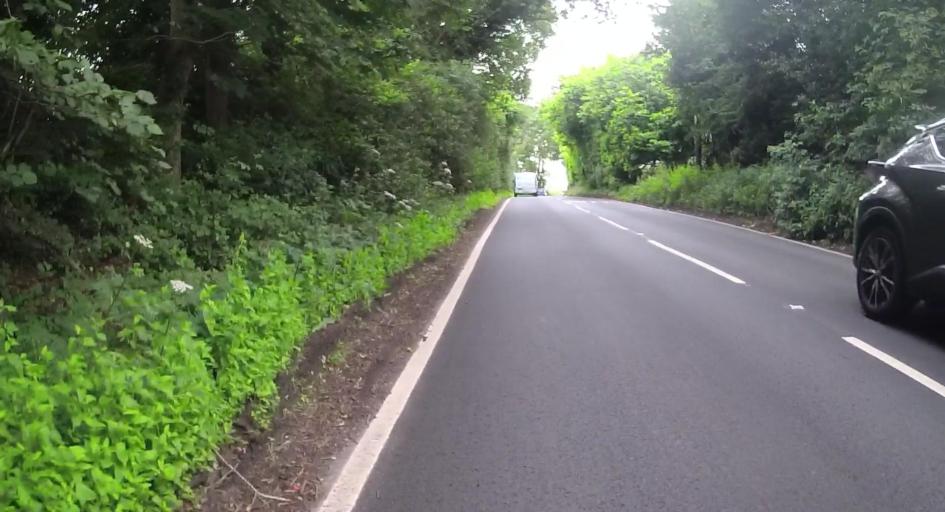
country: GB
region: England
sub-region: Wokingham
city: Barkham
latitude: 51.3911
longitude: -0.8770
